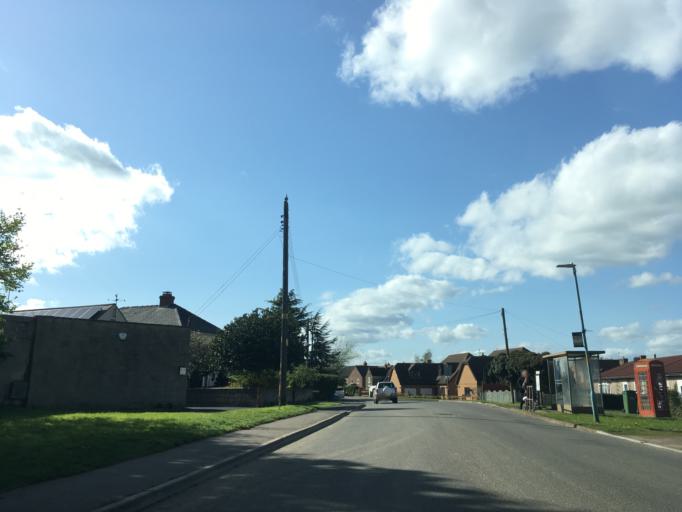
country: GB
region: England
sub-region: Gloucestershire
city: Stonehouse
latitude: 51.7314
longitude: -2.2798
